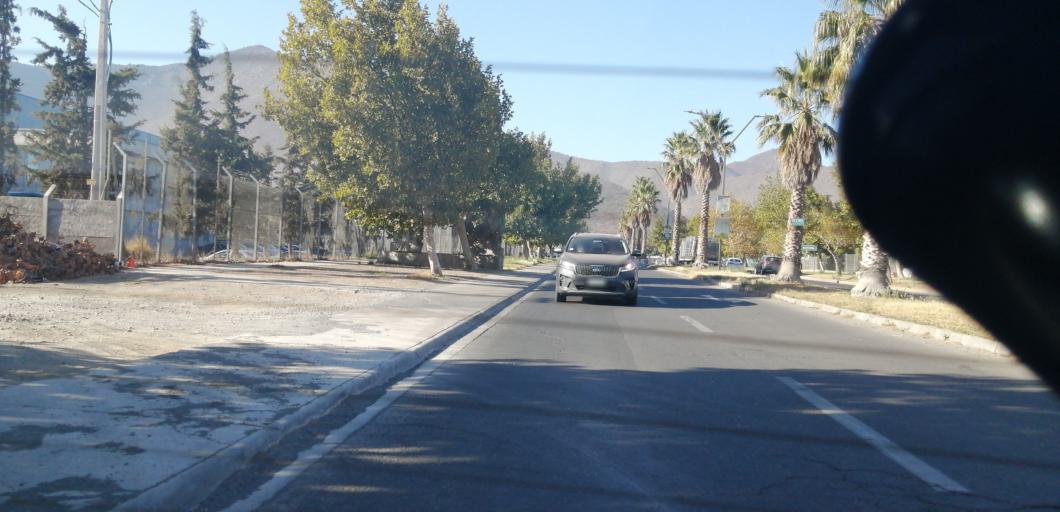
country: CL
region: Santiago Metropolitan
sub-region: Provincia de Santiago
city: Lo Prado
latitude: -33.4450
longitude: -70.8456
